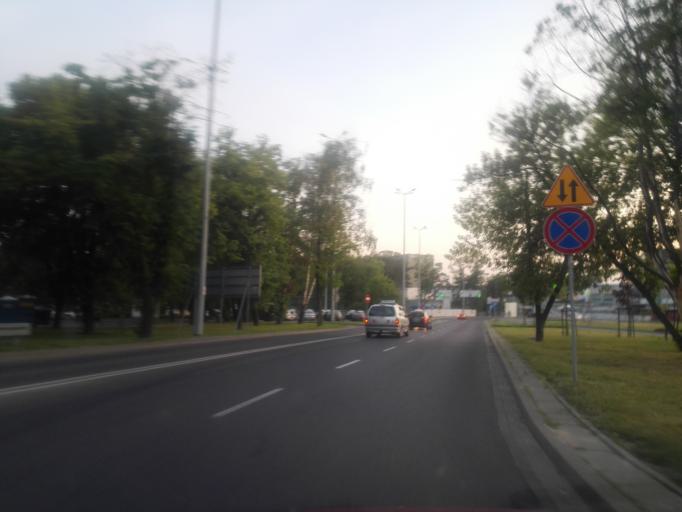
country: PL
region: Masovian Voivodeship
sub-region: Warszawa
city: Wlochy
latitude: 52.1729
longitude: 20.9787
